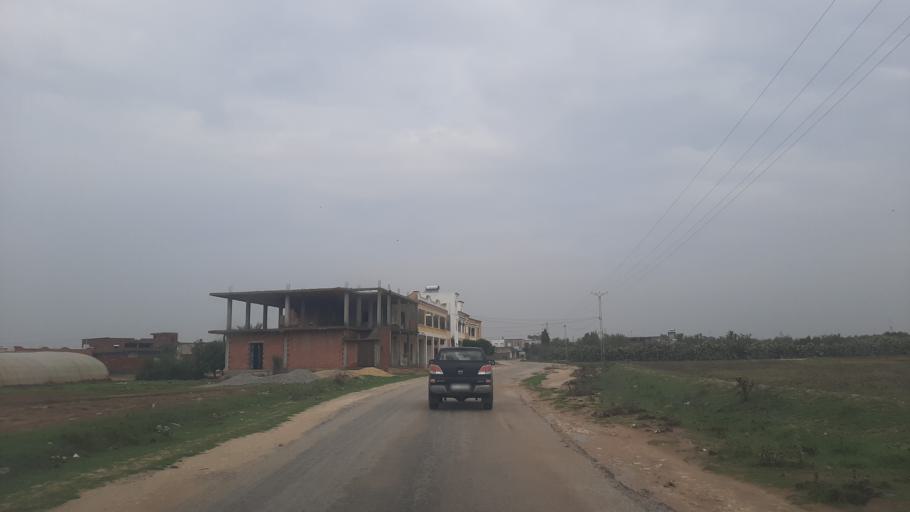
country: TN
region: Al Munastir
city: Sidi Bin Nur
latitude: 35.4750
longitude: 10.8767
